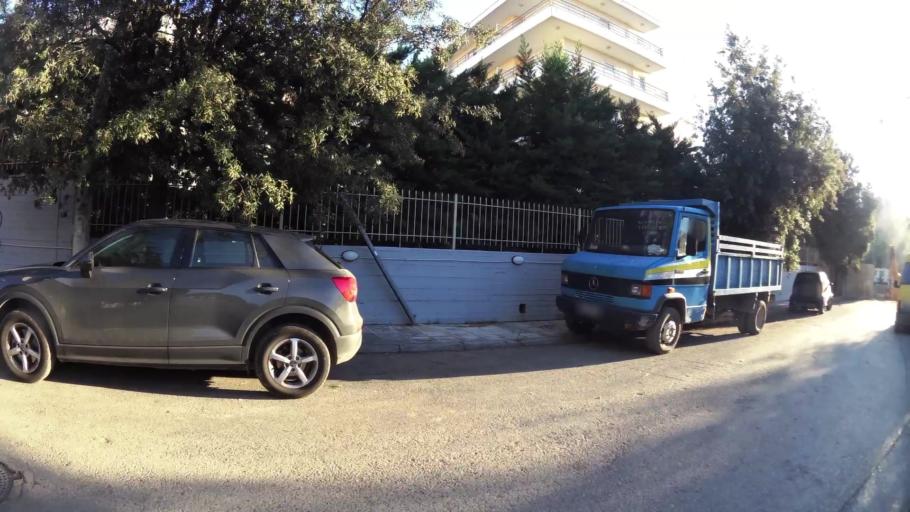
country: GR
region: Attica
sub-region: Nomarchia Athinas
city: Marousi
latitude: 38.0477
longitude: 23.7978
